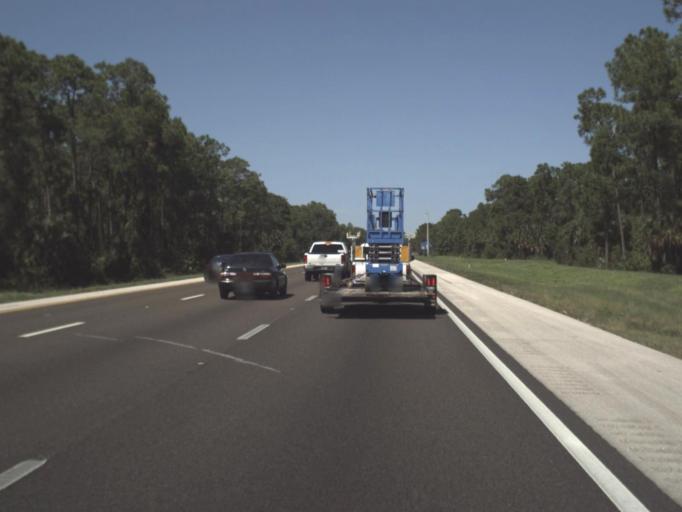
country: US
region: Florida
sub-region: Collier County
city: Vineyards
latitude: 26.2546
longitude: -81.7398
